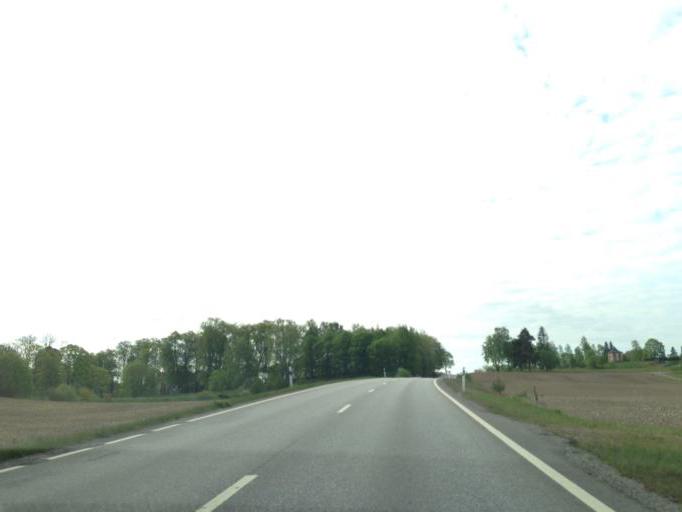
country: SE
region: Soedermanland
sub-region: Flens Kommun
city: Malmkoping
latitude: 59.0912
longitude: 16.8072
